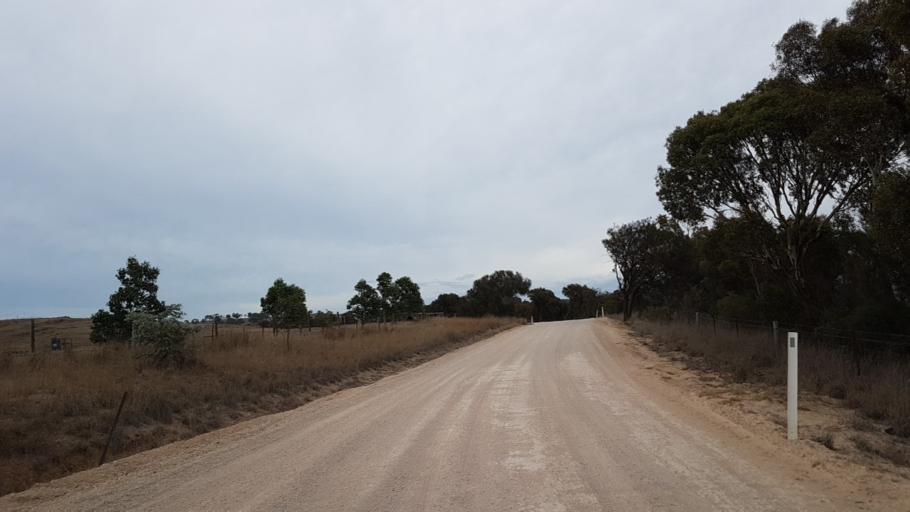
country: AU
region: South Australia
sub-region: Mount Barker
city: Nairne
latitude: -35.0025
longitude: 139.0003
